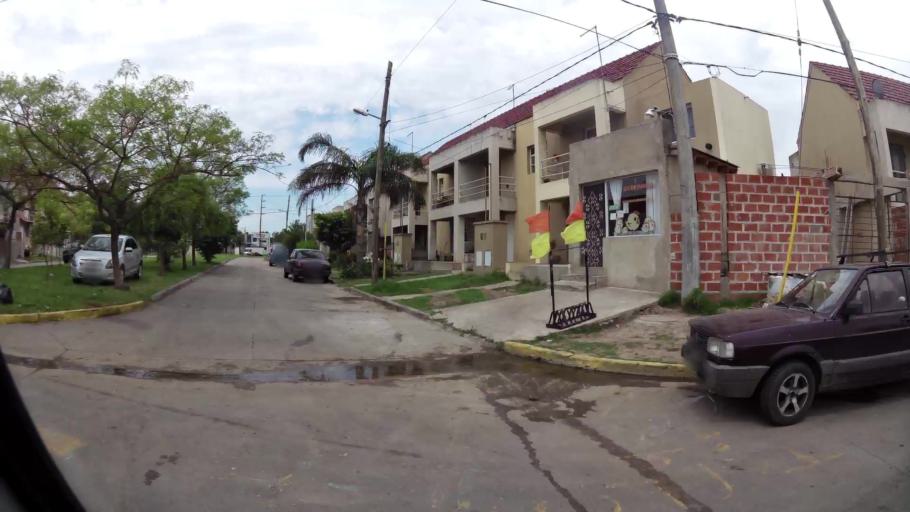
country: AR
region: Buenos Aires
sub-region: Partido de La Plata
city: La Plata
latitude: -34.9055
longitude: -57.9882
